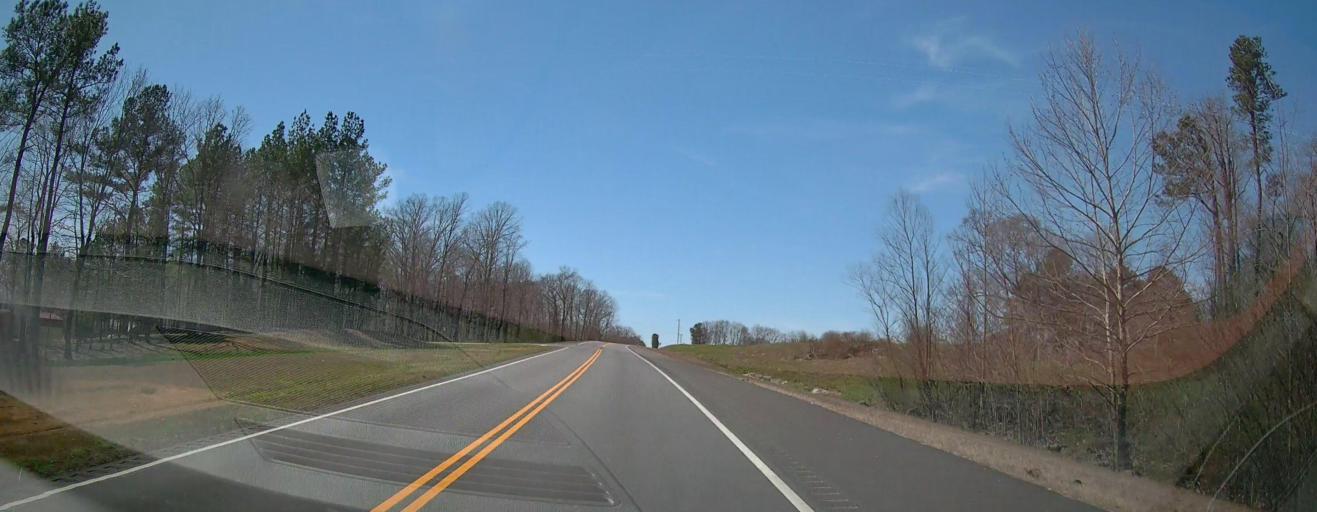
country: US
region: Alabama
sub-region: Blount County
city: Blountsville
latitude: 34.1739
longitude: -86.5643
